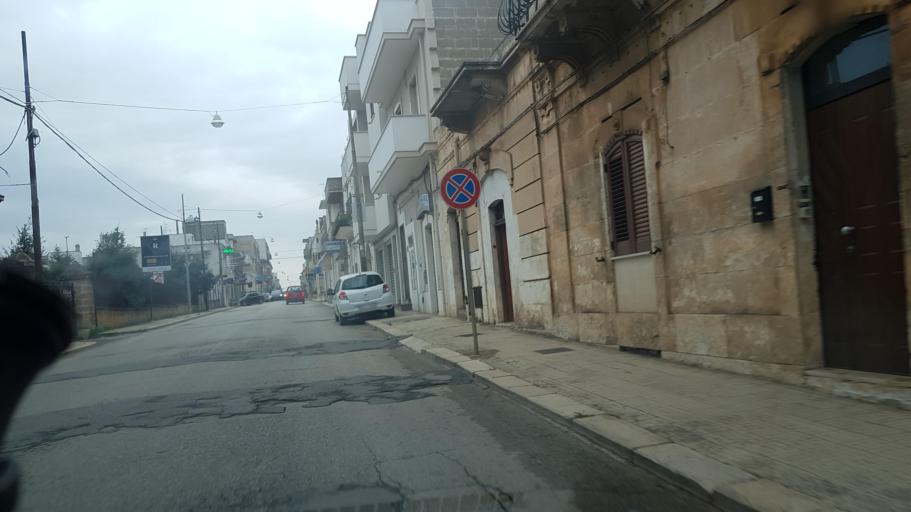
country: IT
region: Apulia
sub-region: Provincia di Brindisi
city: Carovigno
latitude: 40.7028
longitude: 17.6594
